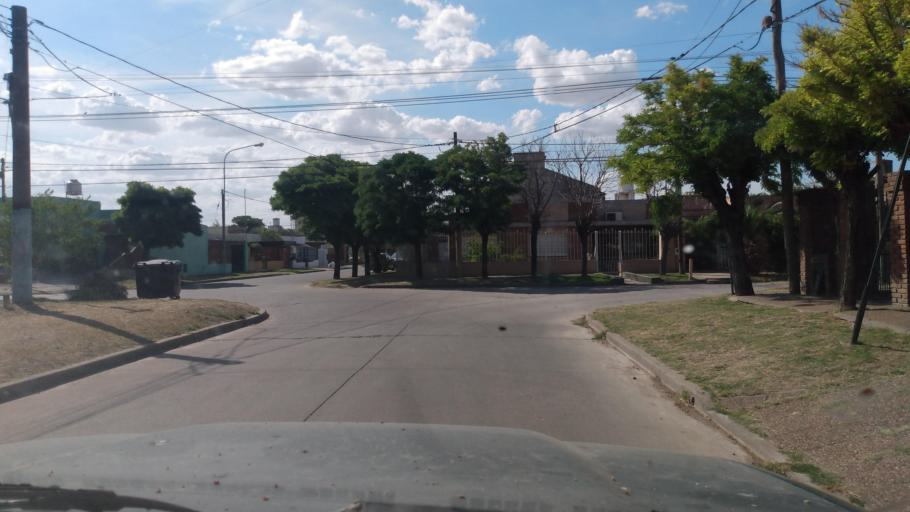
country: AR
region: Buenos Aires
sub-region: Partido de Lujan
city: Lujan
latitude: -34.5582
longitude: -59.1070
